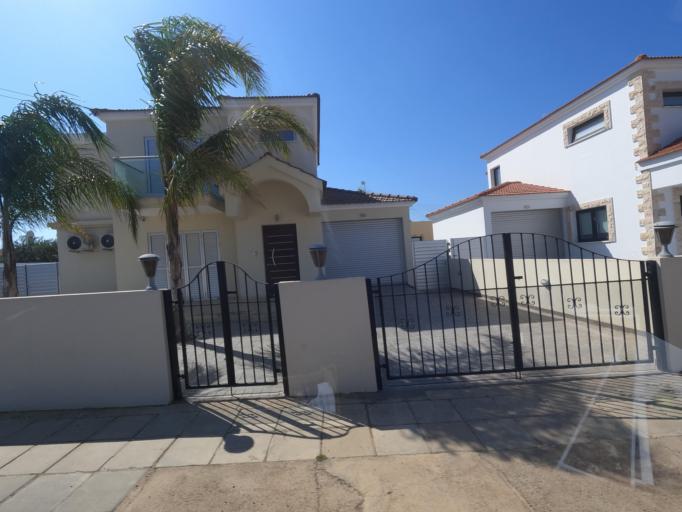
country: CY
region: Ammochostos
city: Frenaros
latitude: 35.0279
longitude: 33.9418
